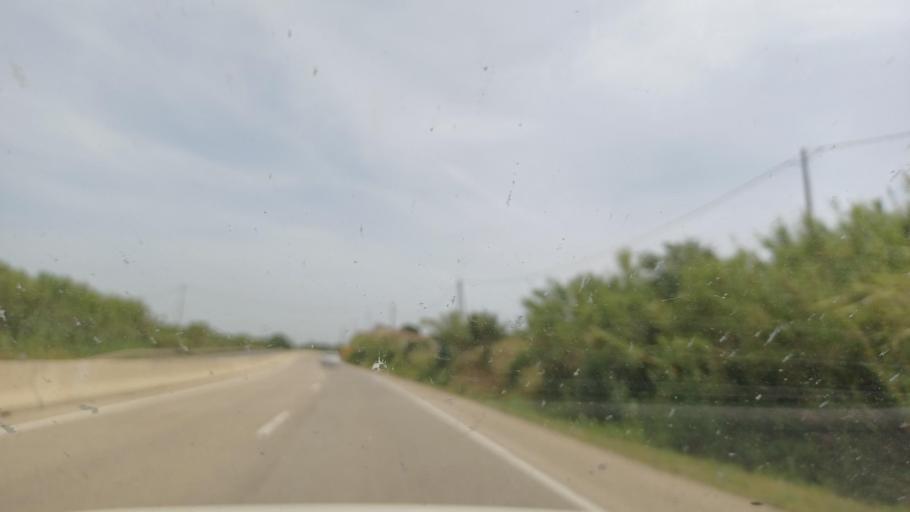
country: ES
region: Catalonia
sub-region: Provincia de Tarragona
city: Vila-seca
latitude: 41.1296
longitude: 1.1479
